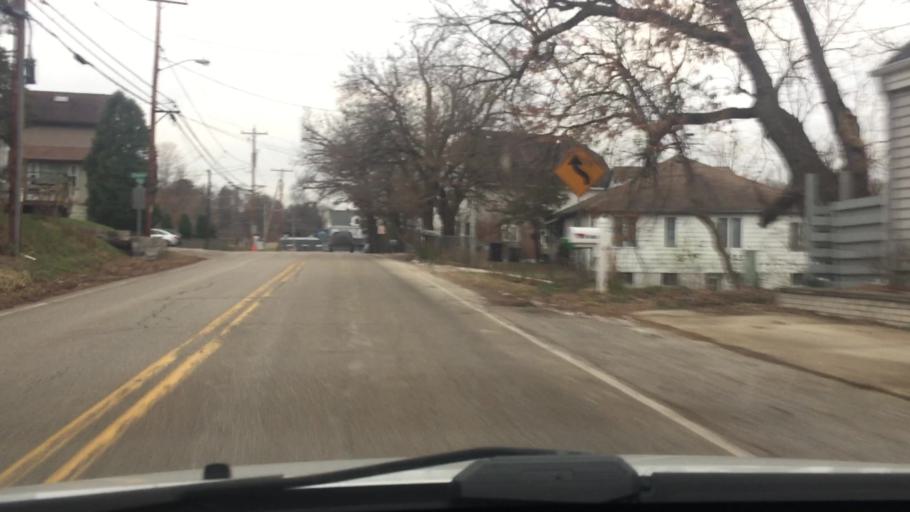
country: US
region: Wisconsin
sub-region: Waukesha County
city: Pewaukee
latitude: 43.0628
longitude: -88.3026
